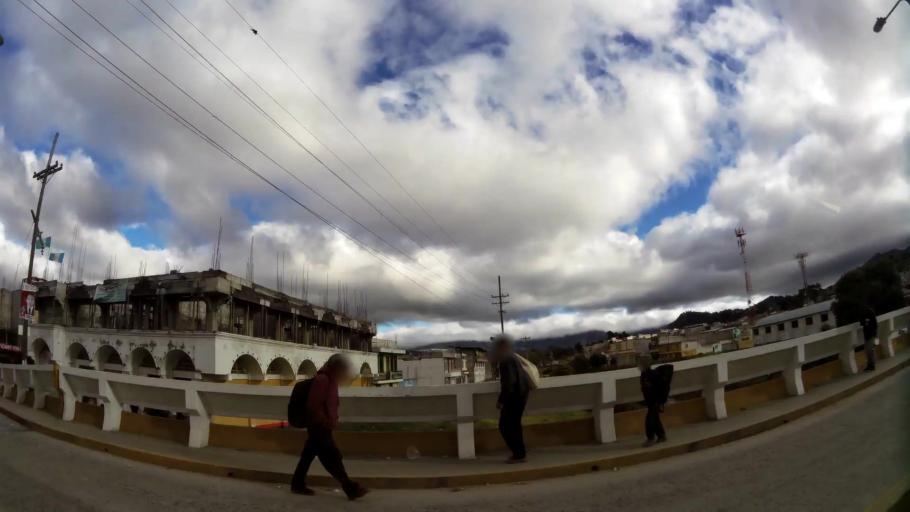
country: GT
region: Quetzaltenango
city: Salcaja
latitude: 14.8798
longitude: -91.4565
